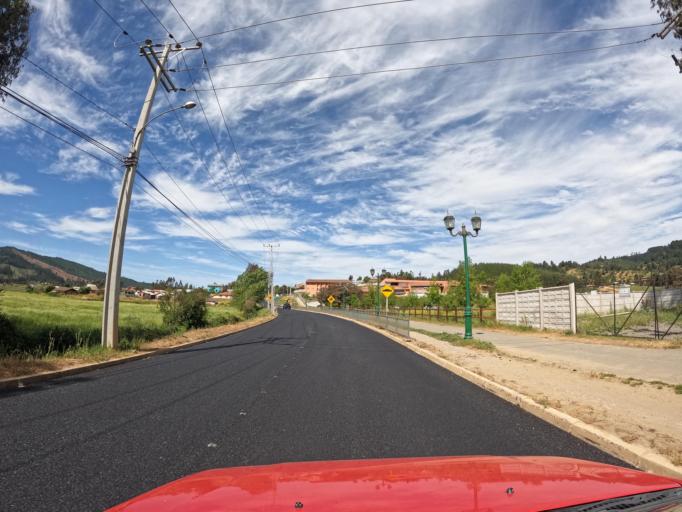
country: CL
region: Maule
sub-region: Provincia de Talca
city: Constitucion
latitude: -35.0982
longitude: -72.0140
